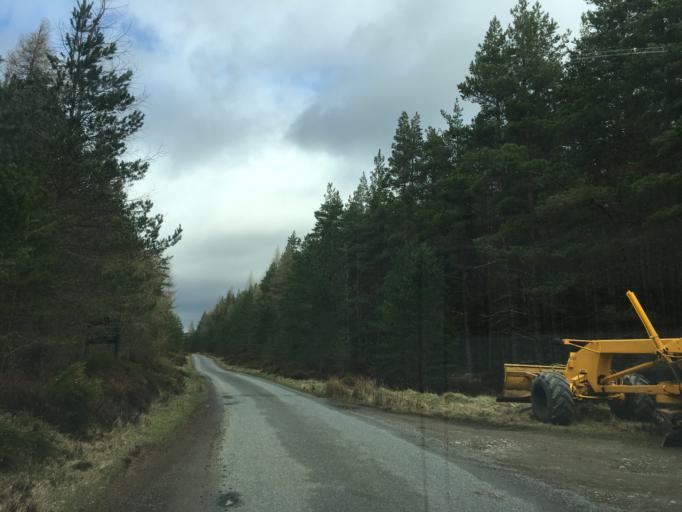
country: GB
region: Scotland
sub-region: Highland
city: Kingussie
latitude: 57.0963
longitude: -3.9187
